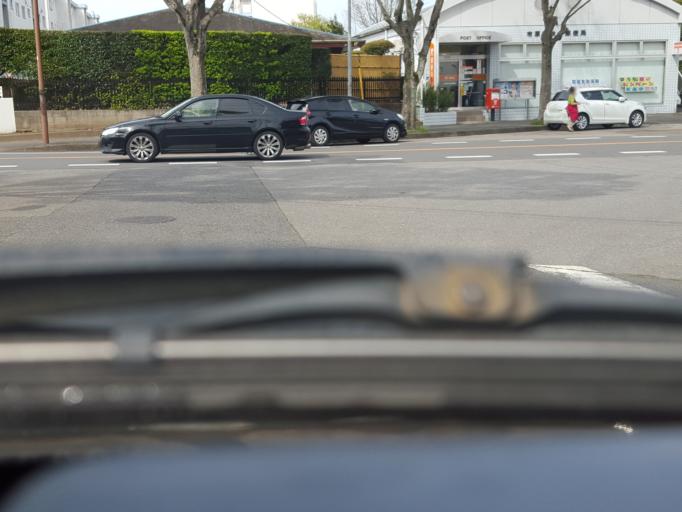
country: JP
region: Chiba
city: Ichihara
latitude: 35.4513
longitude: 140.0528
